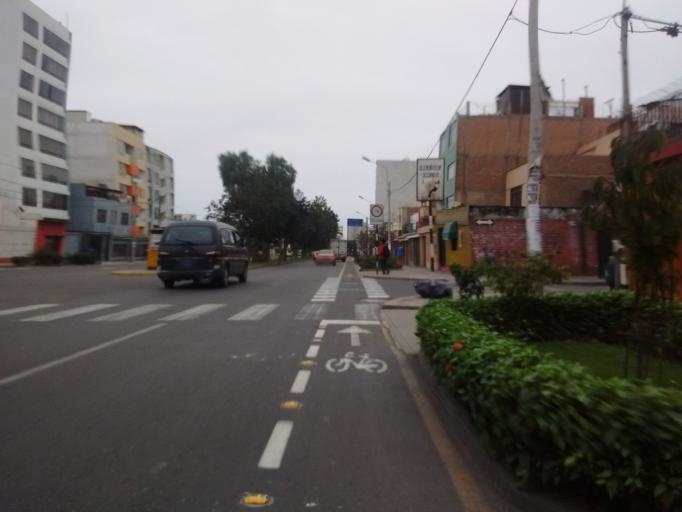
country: PE
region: Callao
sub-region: Callao
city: Callao
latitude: -12.0677
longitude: -77.0714
